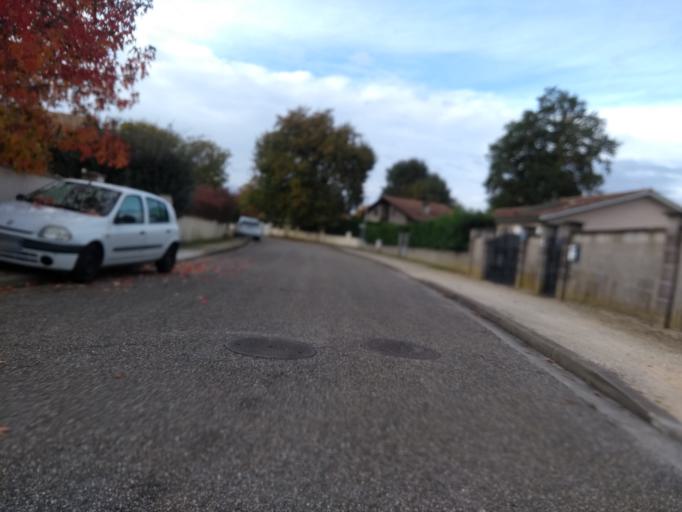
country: FR
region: Aquitaine
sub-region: Departement de la Gironde
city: Canejan
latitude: 44.7644
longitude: -0.6491
